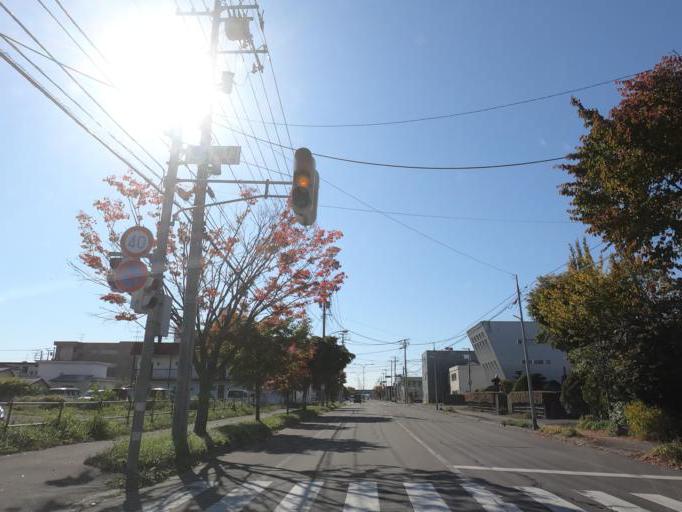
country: JP
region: Hokkaido
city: Obihiro
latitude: 42.9187
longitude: 143.2121
